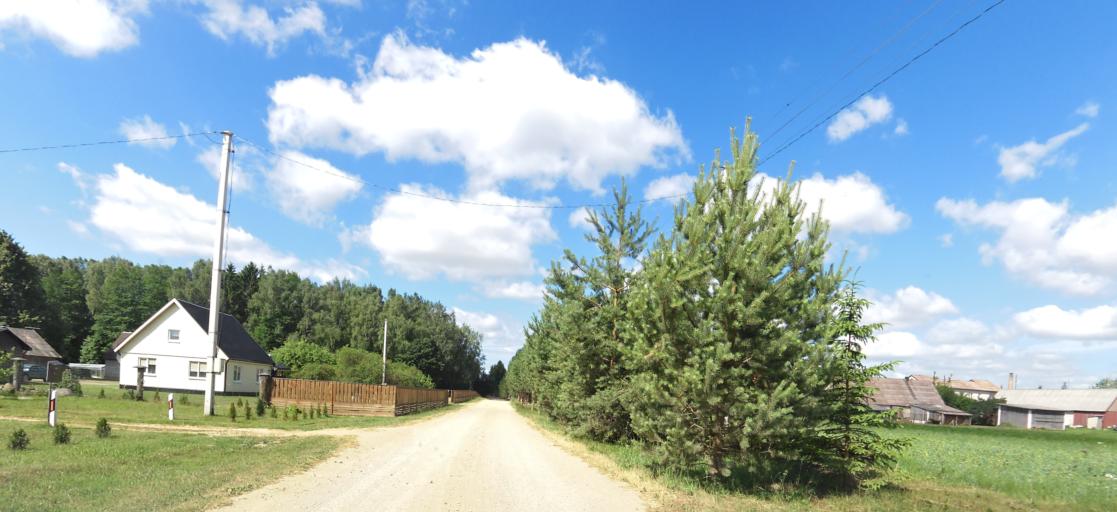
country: LT
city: Vabalninkas
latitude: 56.0209
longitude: 24.8099
